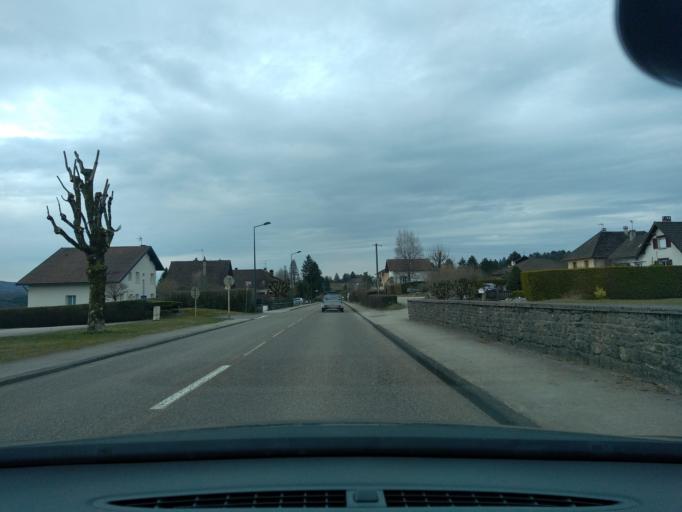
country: FR
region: Franche-Comte
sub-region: Departement du Jura
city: Orgelet
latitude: 46.5191
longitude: 5.6094
